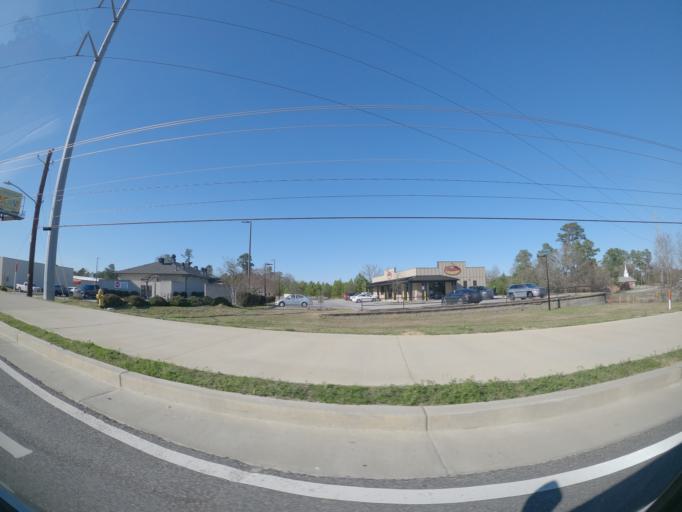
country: US
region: Georgia
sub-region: Columbia County
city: Grovetown
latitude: 33.4578
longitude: -82.1984
